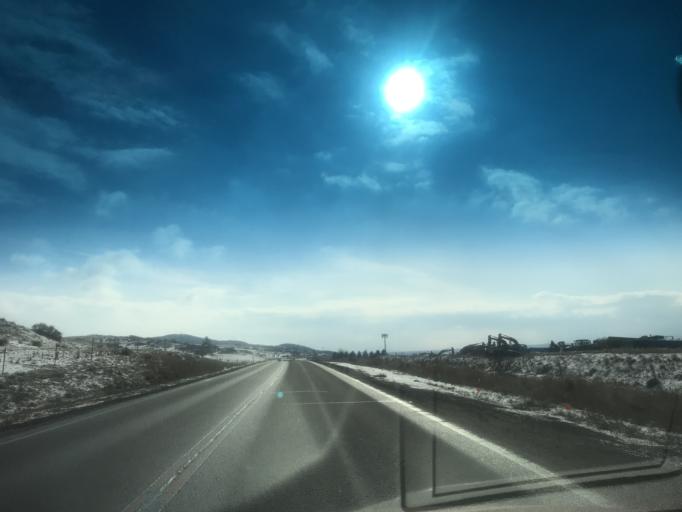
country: US
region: Colorado
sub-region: Douglas County
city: Highlands Ranch
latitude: 39.4759
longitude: -104.9913
